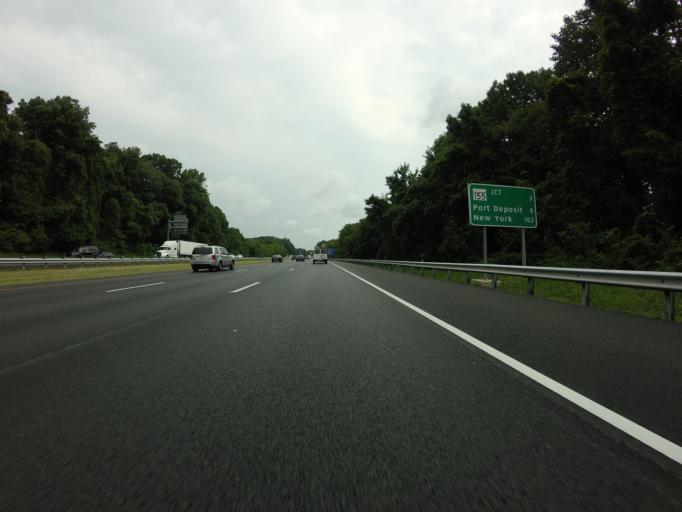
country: US
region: Maryland
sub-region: Harford County
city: Aberdeen
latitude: 39.5370
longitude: -76.1738
